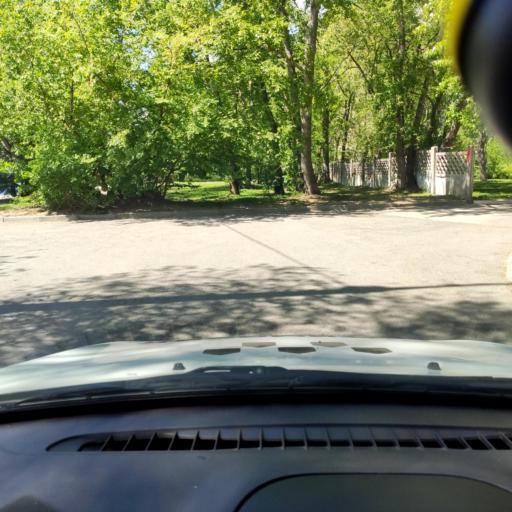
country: RU
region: Samara
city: Zhigulevsk
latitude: 53.4650
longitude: 49.5286
